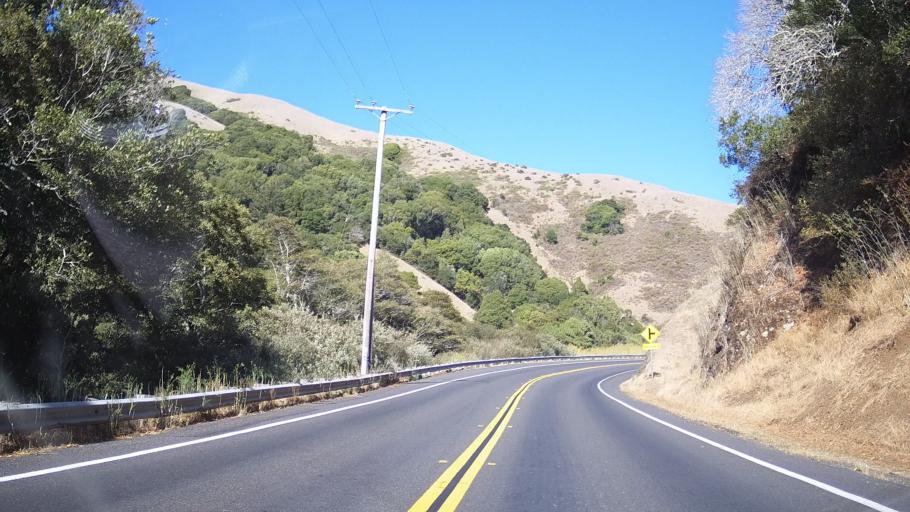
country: US
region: California
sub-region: Marin County
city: Lagunitas-Forest Knolls
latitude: 38.0703
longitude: -122.7625
